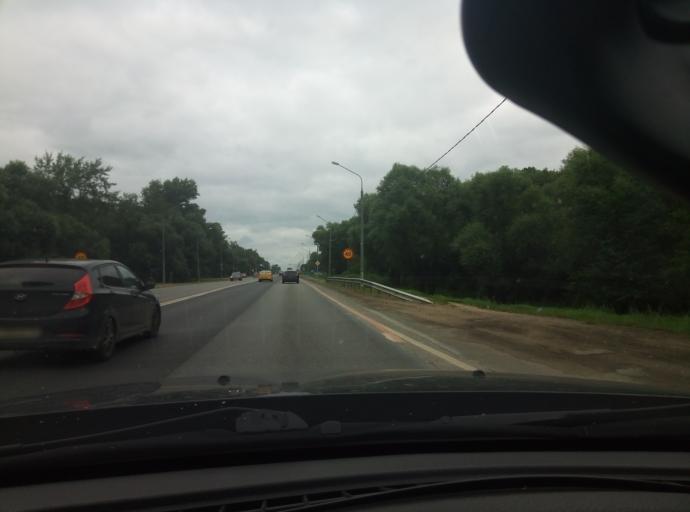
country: RU
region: Kaluga
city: Obninsk
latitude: 55.0977
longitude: 36.6380
